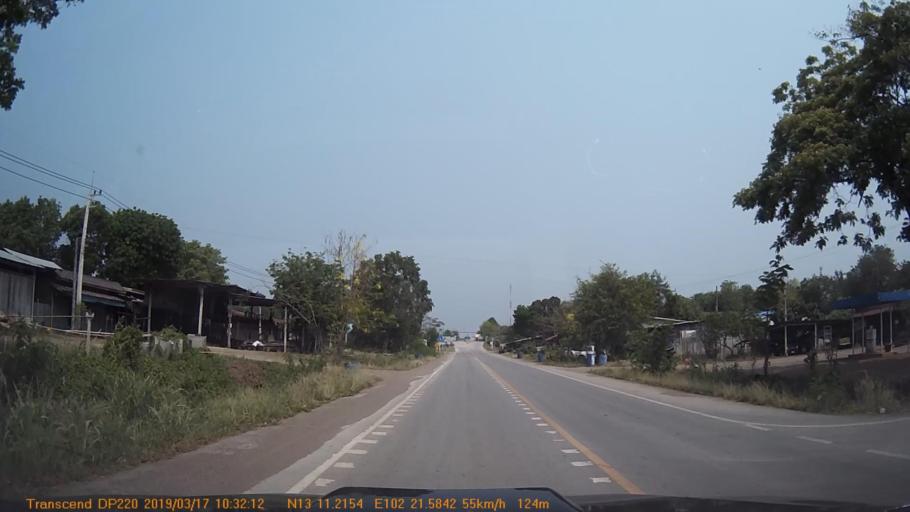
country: TH
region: Chanthaburi
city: Soi Dao
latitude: 13.1872
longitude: 102.3596
